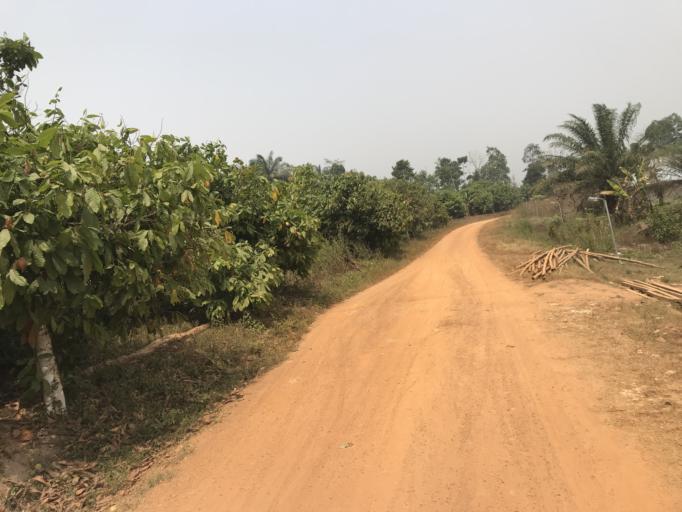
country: NG
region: Osun
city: Ifetedo
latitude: 7.0411
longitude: 4.4605
